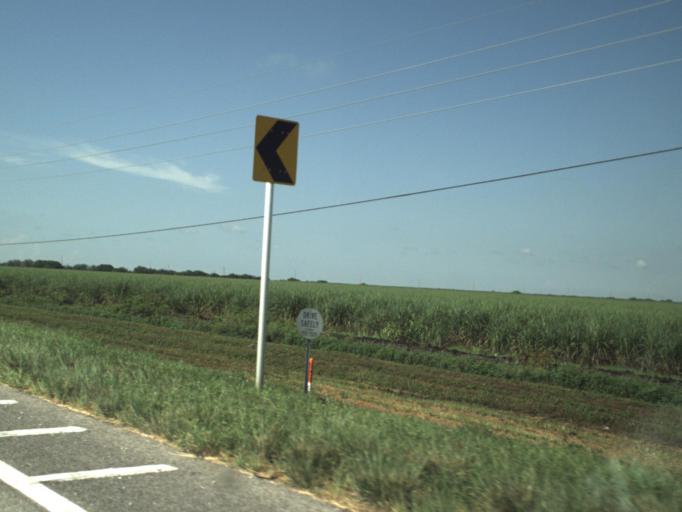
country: US
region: Florida
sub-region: Palm Beach County
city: Belle Glade Camp
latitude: 26.5587
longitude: -80.7107
